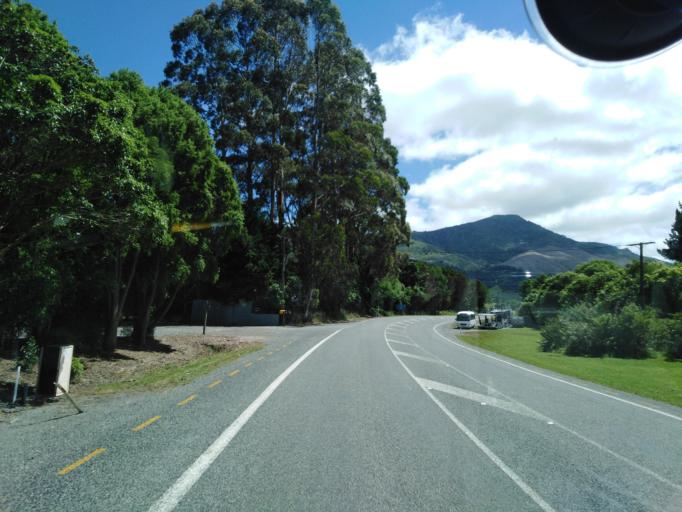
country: NZ
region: Nelson
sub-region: Nelson City
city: Nelson
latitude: -41.2162
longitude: 173.3953
